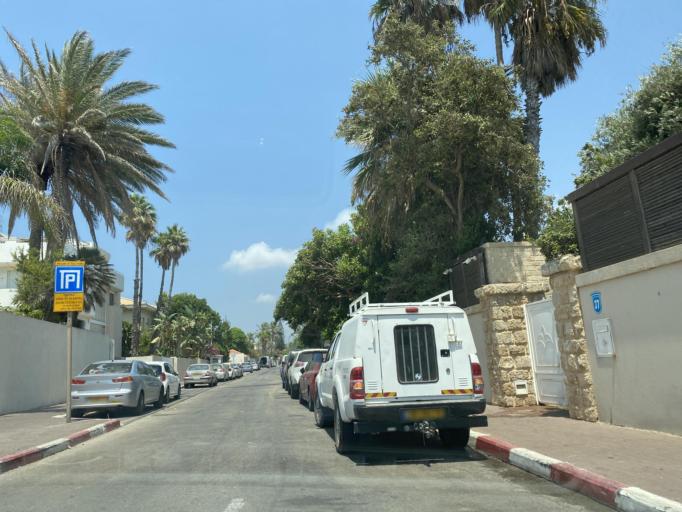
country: IL
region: Tel Aviv
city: Herzliya Pituah
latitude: 32.1805
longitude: 34.8042
